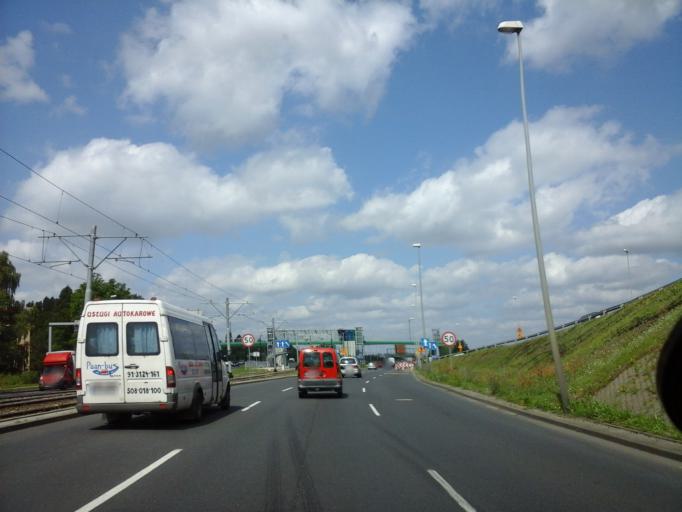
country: PL
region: West Pomeranian Voivodeship
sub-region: Szczecin
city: Szczecin
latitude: 53.3871
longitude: 14.6281
